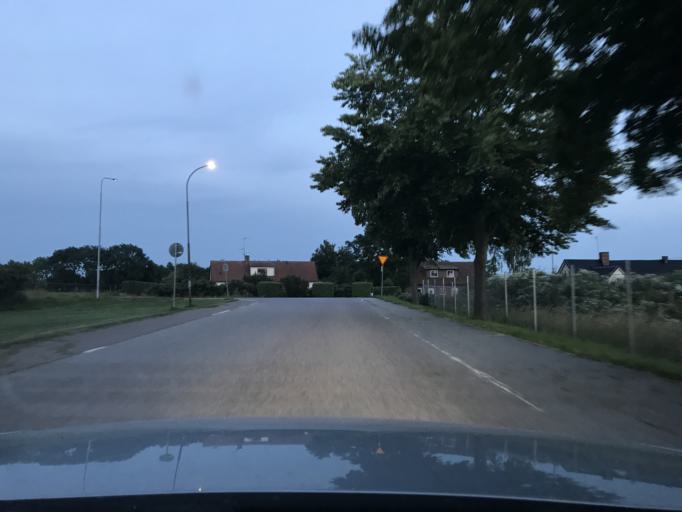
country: SE
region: Skane
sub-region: Svalovs Kommun
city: Svaloev
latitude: 55.9085
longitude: 13.0928
